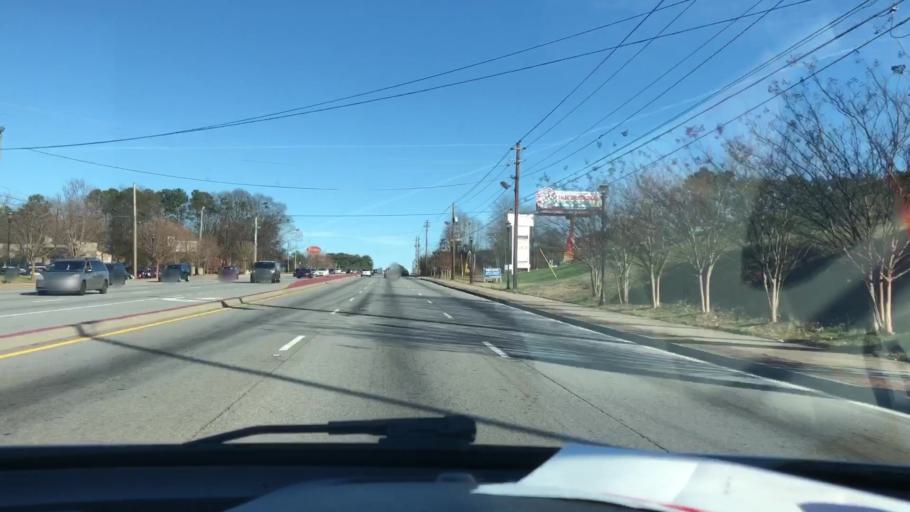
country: US
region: Georgia
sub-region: DeKalb County
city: Clarkston
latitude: 33.8007
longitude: -84.2114
